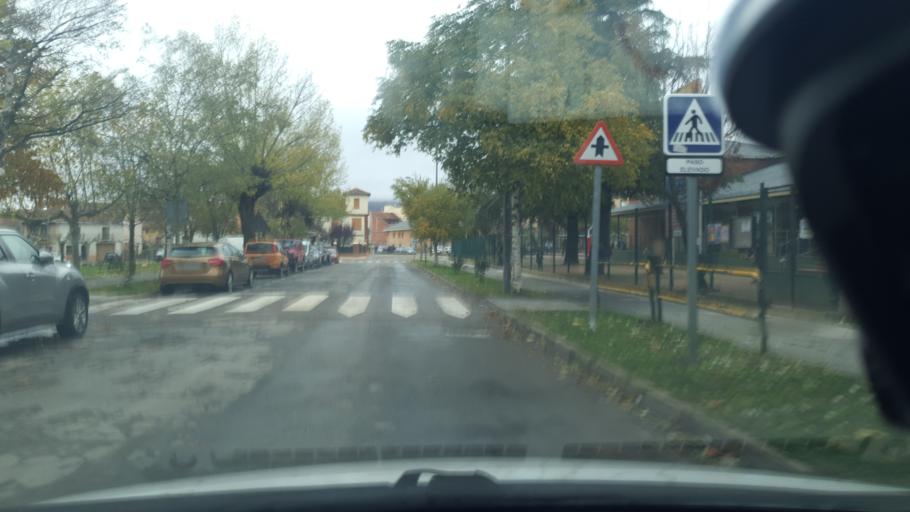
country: ES
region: Castille and Leon
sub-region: Provincia de Segovia
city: Riaza
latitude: 41.2768
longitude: -3.4814
